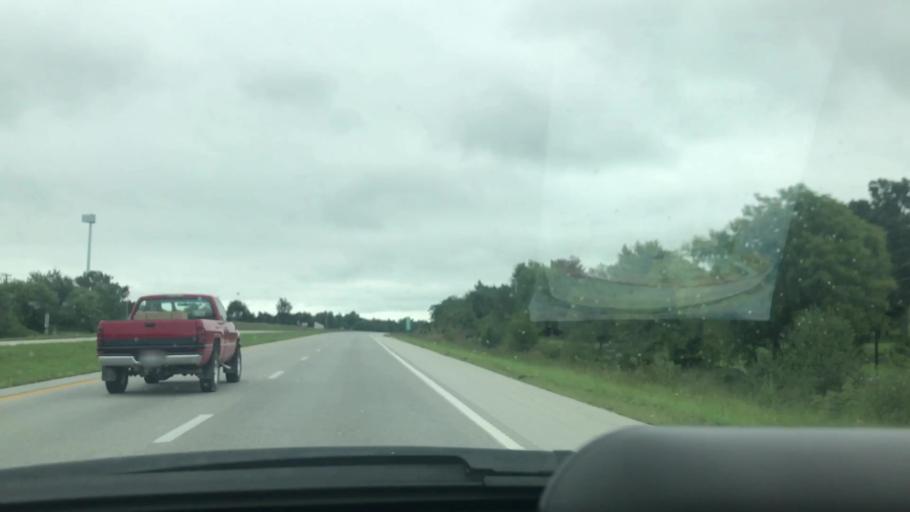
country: US
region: Missouri
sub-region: Greene County
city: Strafford
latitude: 37.2798
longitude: -93.2057
